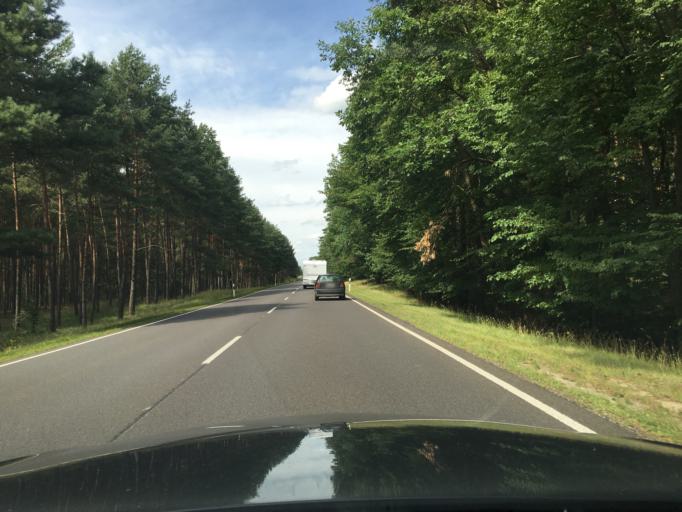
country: DE
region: Brandenburg
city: Furstenberg
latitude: 53.2695
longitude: 13.1148
